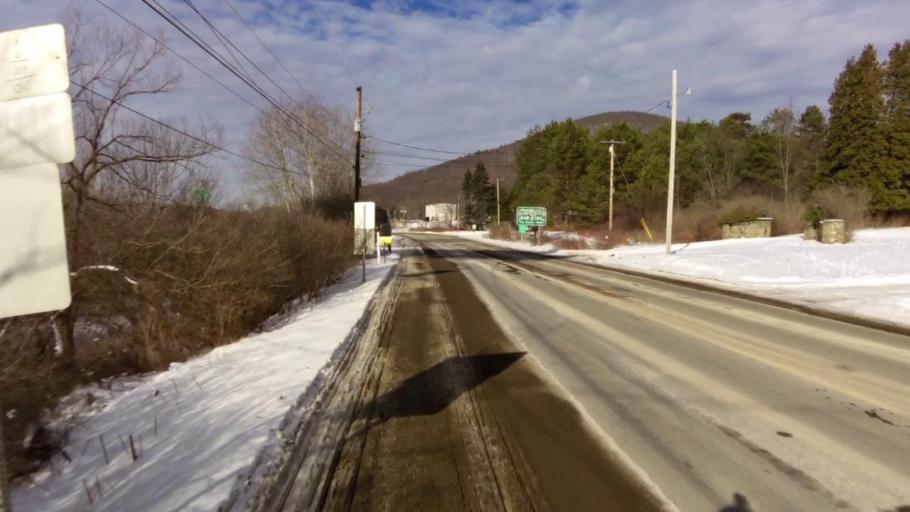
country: US
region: Pennsylvania
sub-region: McKean County
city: Foster Brook
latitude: 41.9997
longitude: -78.6180
